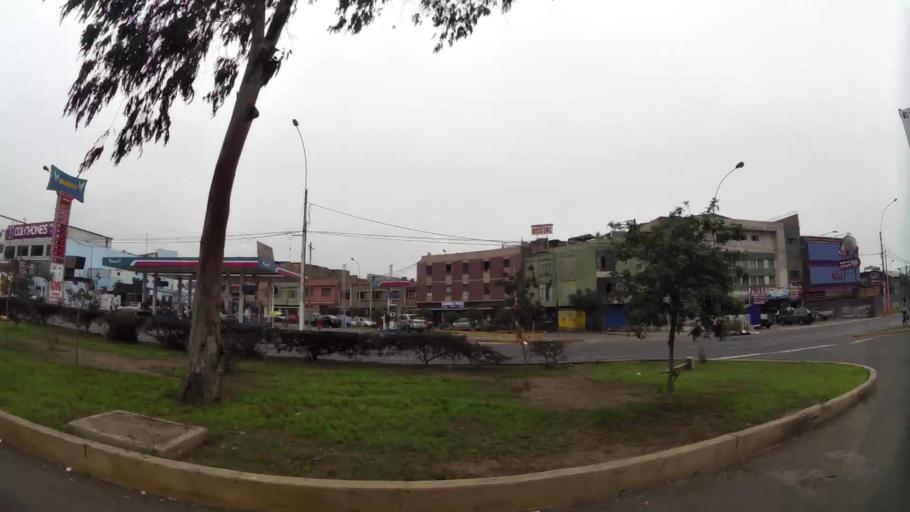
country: PE
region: Lima
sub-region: Lima
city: San Luis
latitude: -12.0746
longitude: -77.0225
